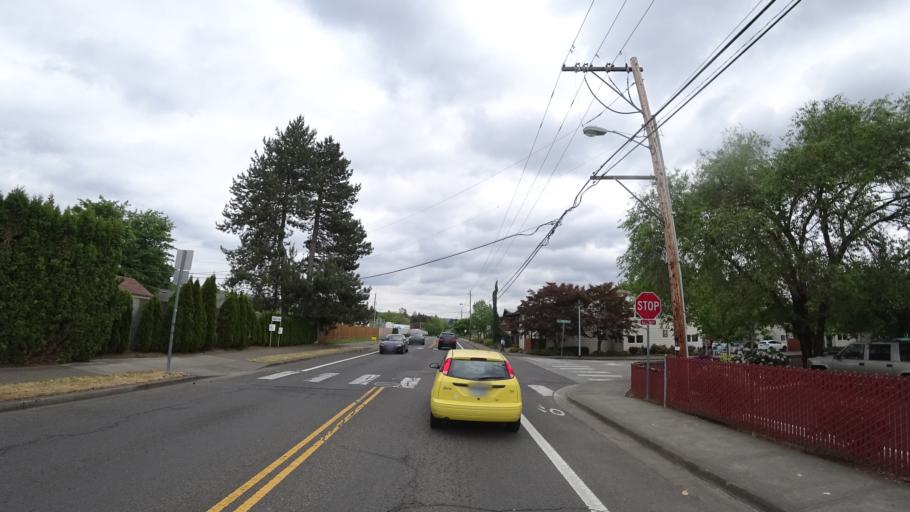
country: US
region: Oregon
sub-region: Washington County
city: Beaverton
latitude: 45.4937
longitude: -122.8032
